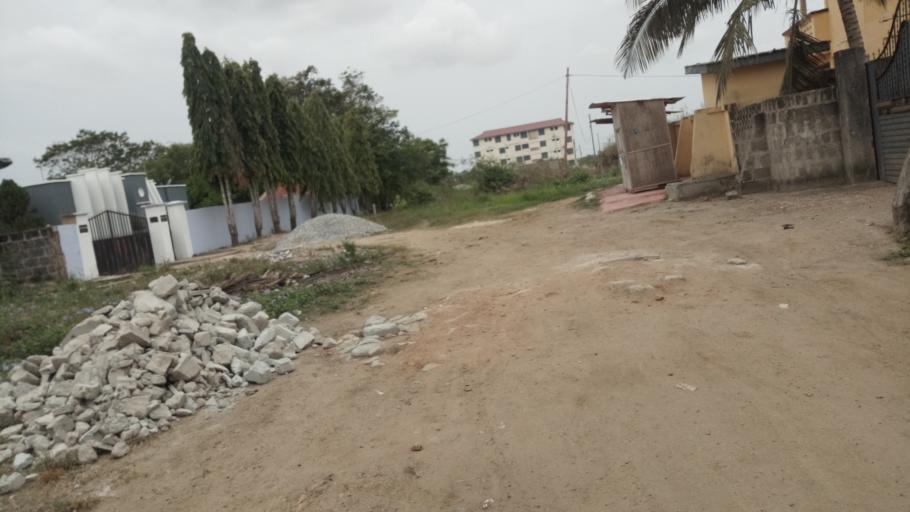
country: GH
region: Central
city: Winneba
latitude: 5.3645
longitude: -0.6383
